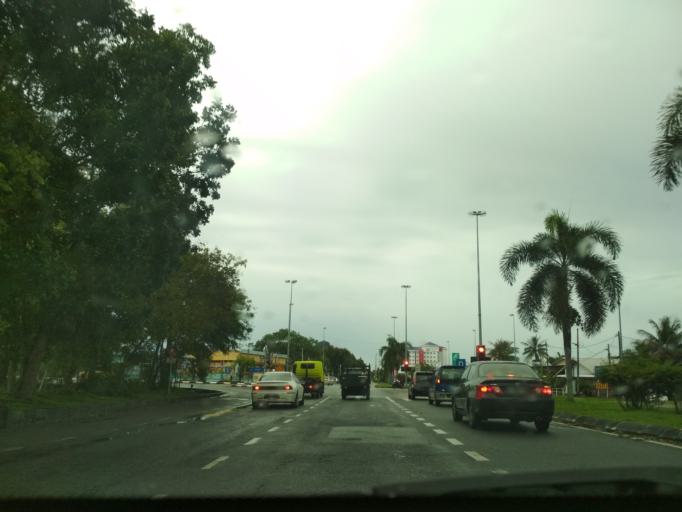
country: MY
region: Perlis
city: Kangar
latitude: 6.4268
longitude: 100.1847
